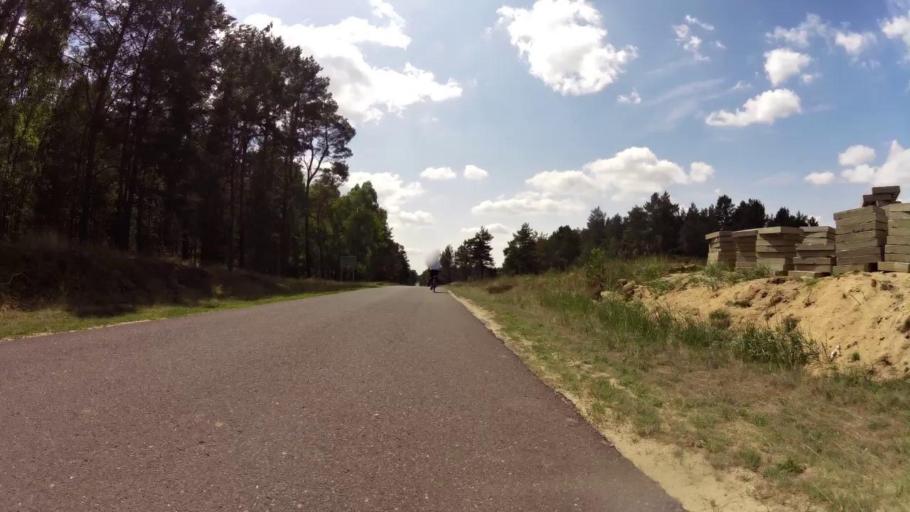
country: PL
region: West Pomeranian Voivodeship
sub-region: Powiat drawski
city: Drawsko Pomorskie
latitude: 53.4069
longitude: 15.7347
